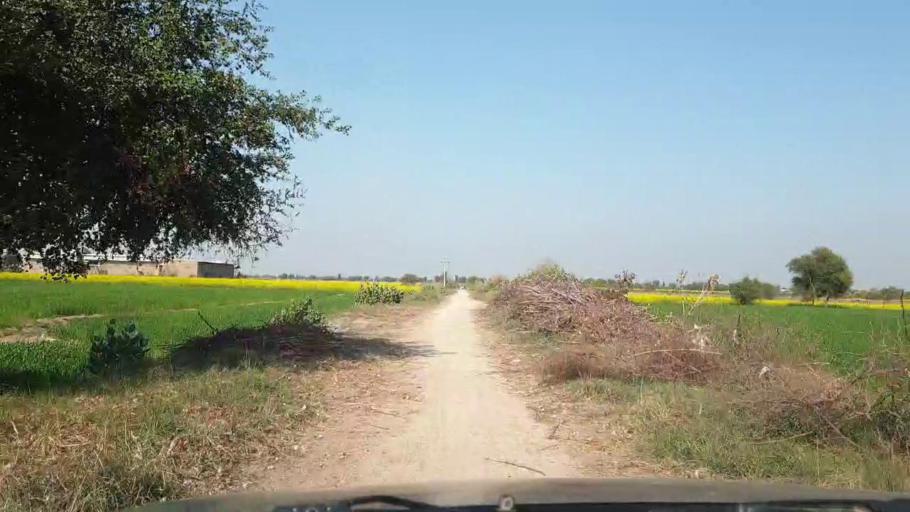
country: PK
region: Sindh
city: Jhol
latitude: 25.9475
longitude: 68.8654
